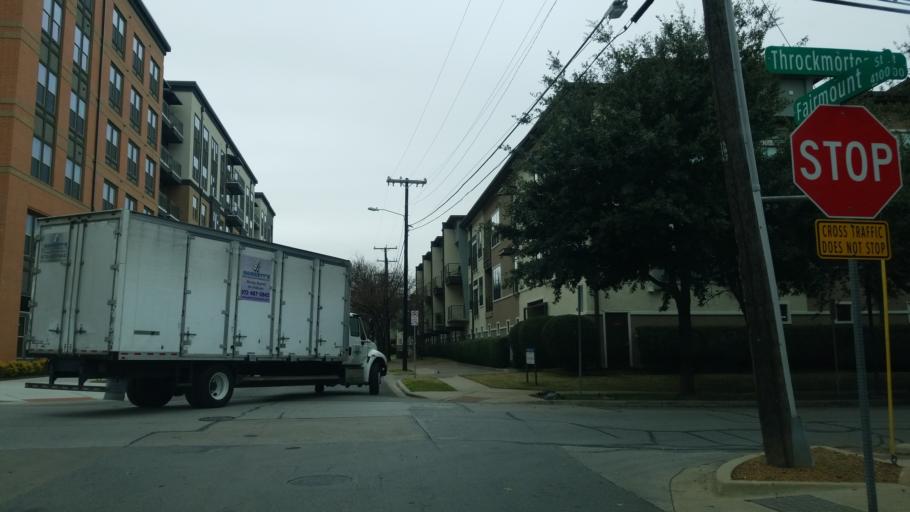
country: US
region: Texas
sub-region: Dallas County
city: Dallas
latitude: 32.8074
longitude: -96.8160
